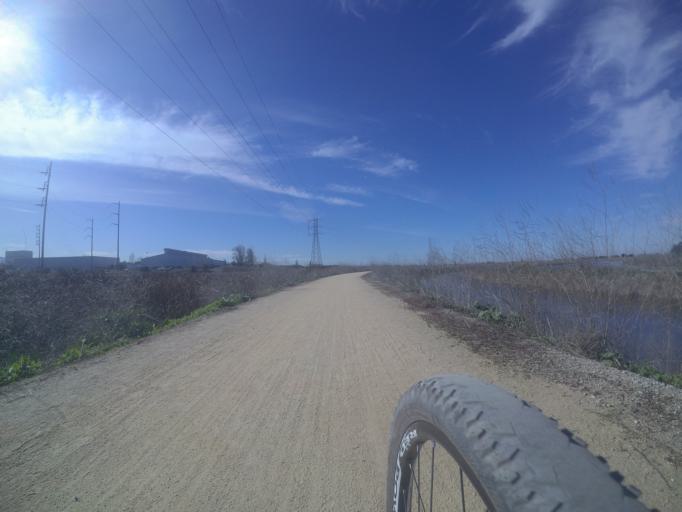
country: US
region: California
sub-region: Santa Clara County
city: Sunnyvale
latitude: 37.4230
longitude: -122.0258
